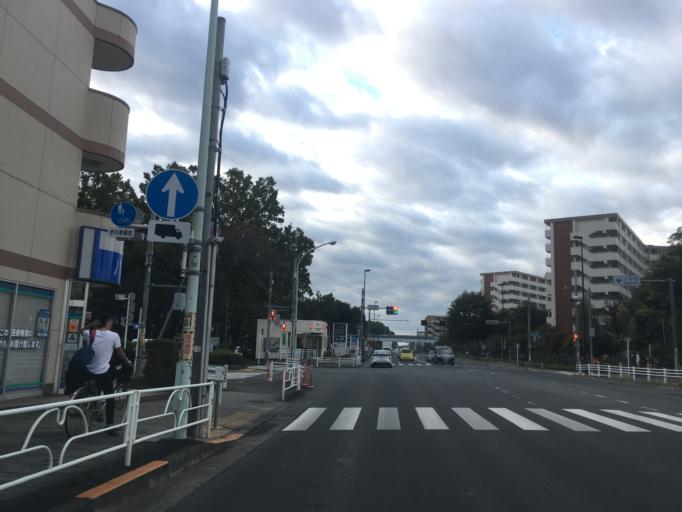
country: JP
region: Tokyo
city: Higashimurayama-shi
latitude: 35.7444
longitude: 139.4669
